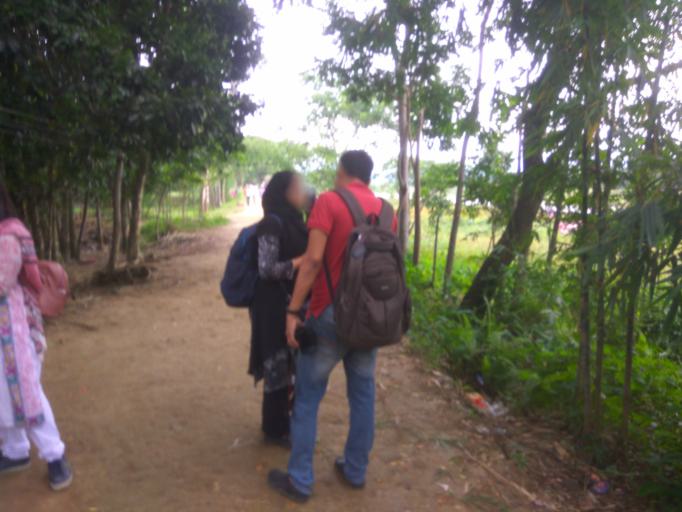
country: IN
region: Assam
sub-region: Karimganj
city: Karimganj
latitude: 24.9956
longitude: 92.3868
